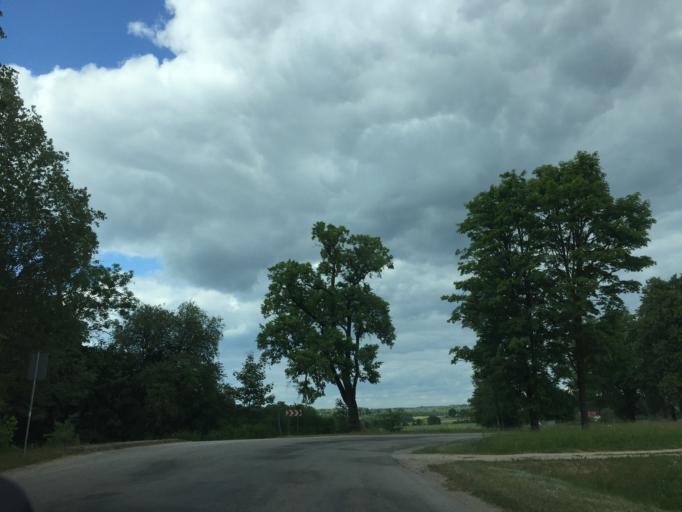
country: LV
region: Skriveri
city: Skriveri
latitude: 56.8358
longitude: 25.1323
